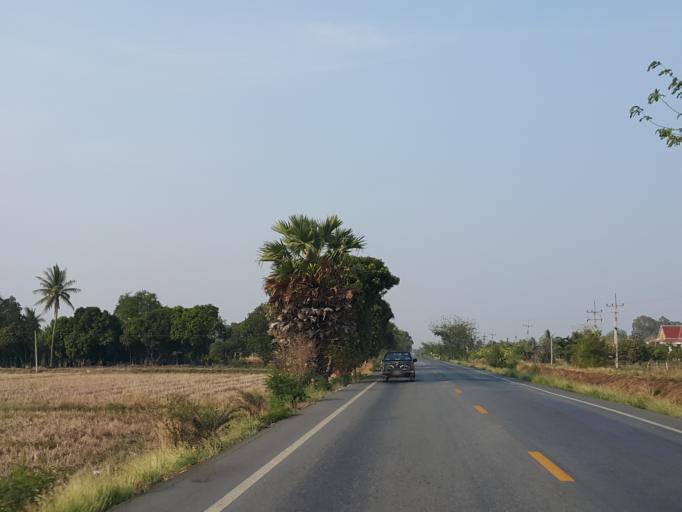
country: TH
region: Chai Nat
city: Sankhaburi
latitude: 14.9851
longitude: 100.1095
